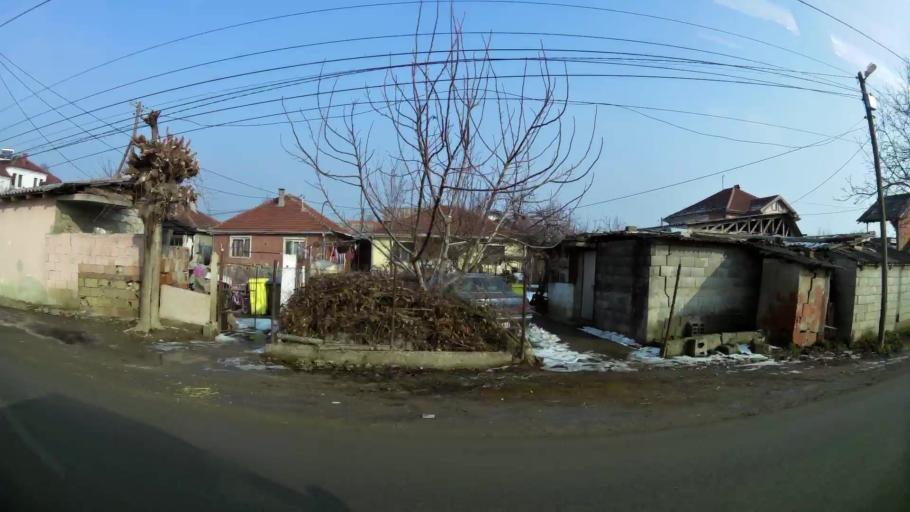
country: MK
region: Ilinden
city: Marino
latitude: 41.9801
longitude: 21.5929
